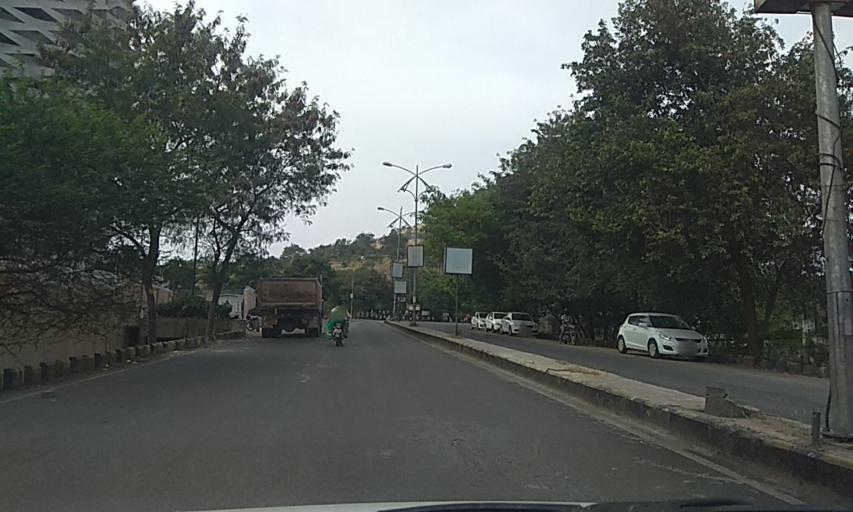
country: IN
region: Maharashtra
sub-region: Pune Division
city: Pimpri
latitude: 18.5974
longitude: 73.7177
